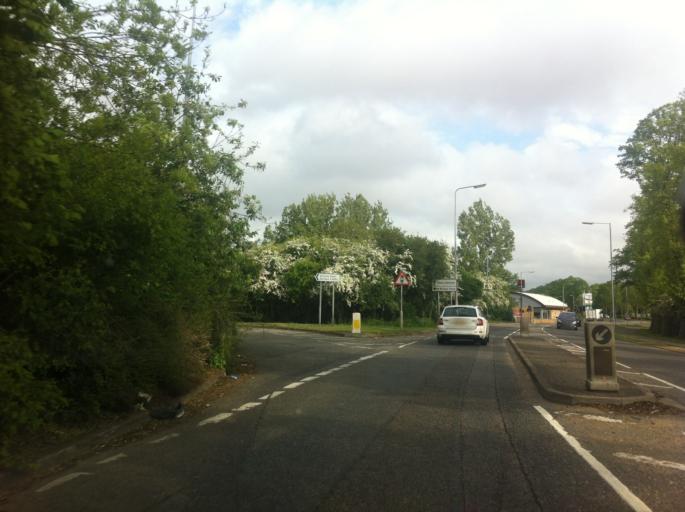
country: GB
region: England
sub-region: Northamptonshire
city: Wellingborough
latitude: 52.2910
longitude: -0.6826
